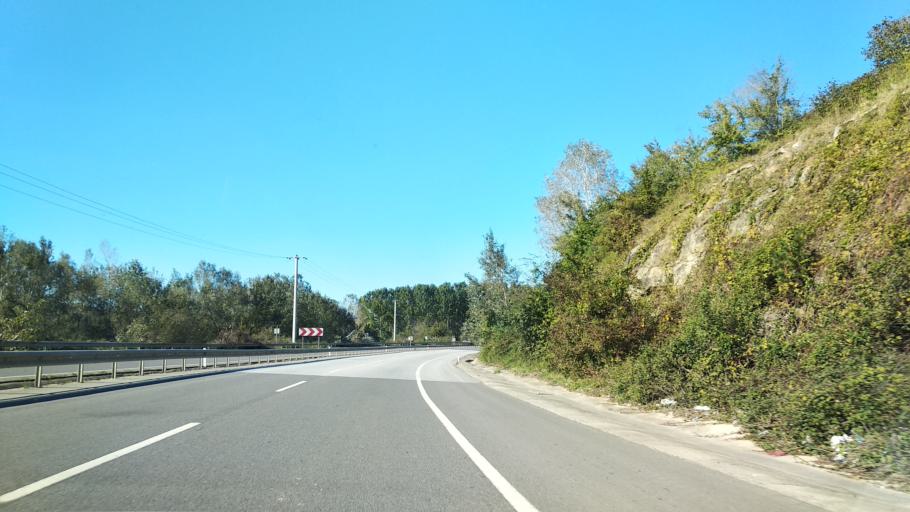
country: TR
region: Sakarya
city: Karasu
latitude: 41.0862
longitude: 30.6473
